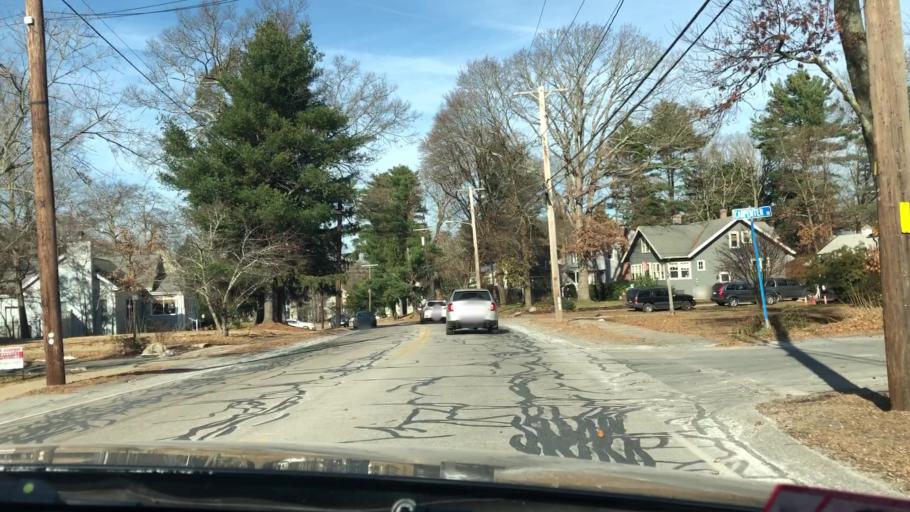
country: US
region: Massachusetts
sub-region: Norfolk County
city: Walpole
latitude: 42.1322
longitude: -71.2438
